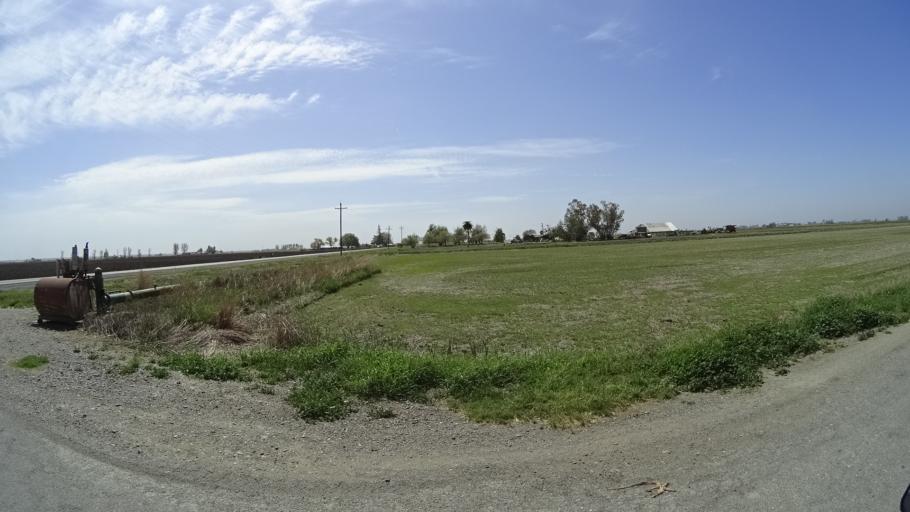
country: US
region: California
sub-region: Glenn County
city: Willows
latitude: 39.5731
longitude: -122.0654
